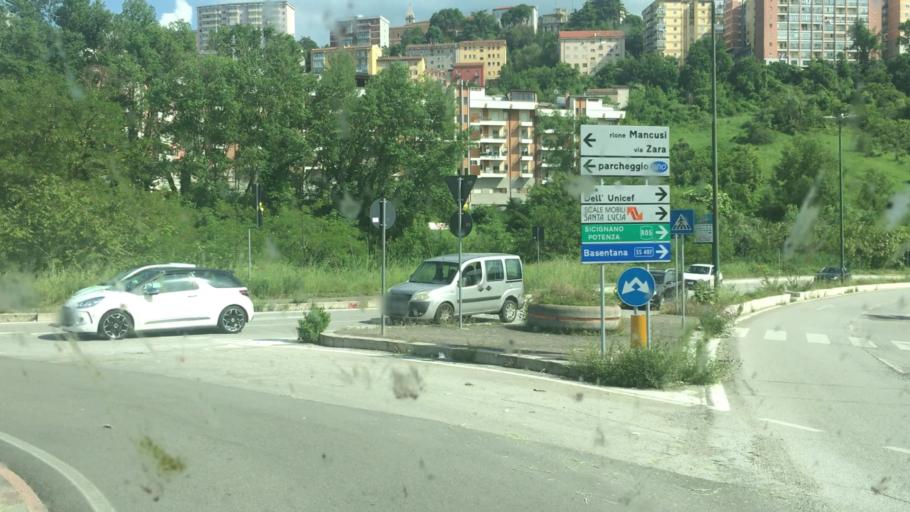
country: IT
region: Basilicate
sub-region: Provincia di Potenza
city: Potenza
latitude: 40.6427
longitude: 15.7996
